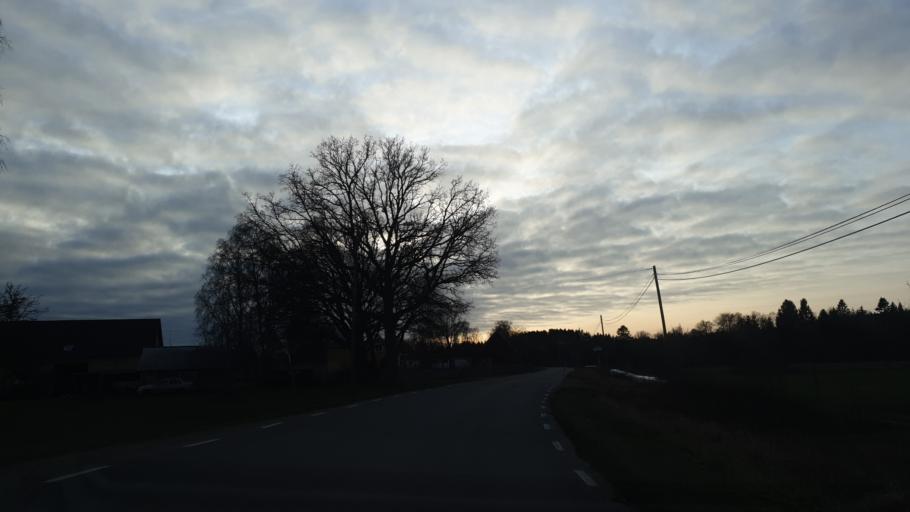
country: SE
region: Blekinge
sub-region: Karlskrona Kommun
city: Jaemjoe
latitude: 56.1841
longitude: 15.9413
